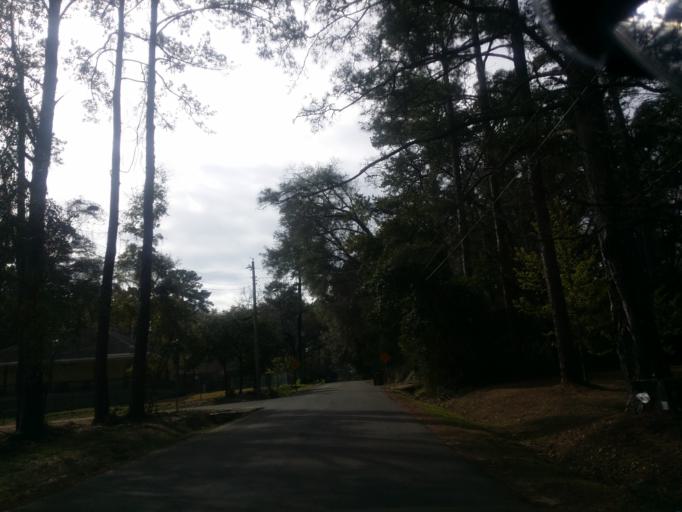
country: US
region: Florida
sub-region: Leon County
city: Tallahassee
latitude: 30.4476
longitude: -84.2401
